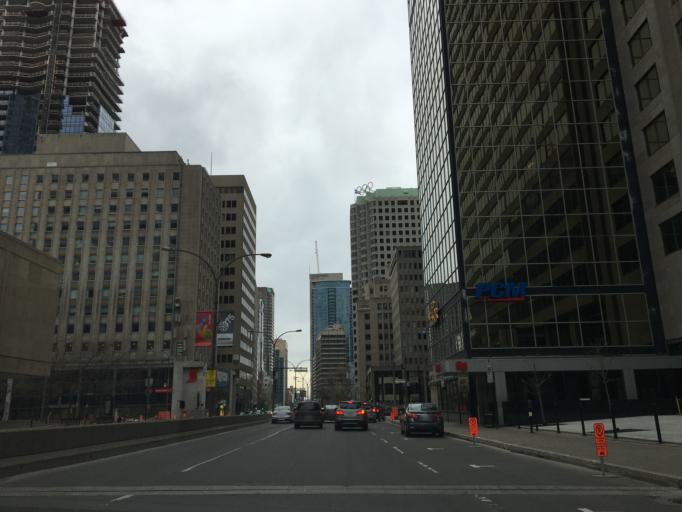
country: CA
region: Quebec
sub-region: Montreal
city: Montreal
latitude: 45.5012
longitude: -73.5680
